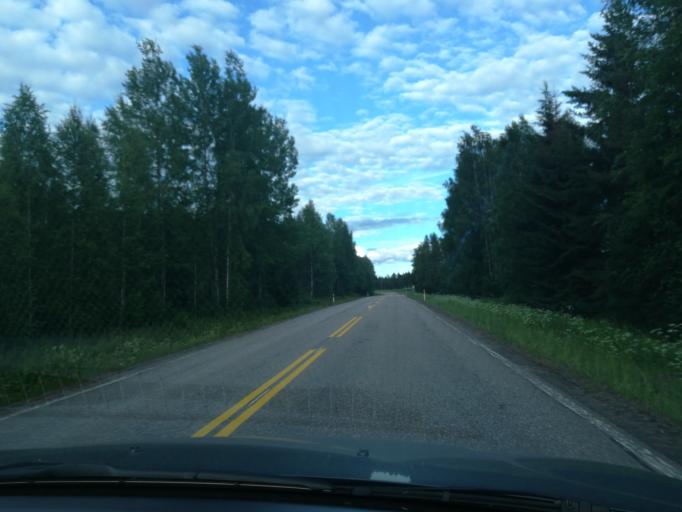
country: FI
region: Southern Savonia
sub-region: Mikkeli
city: Puumala
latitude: 61.5009
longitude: 27.8528
